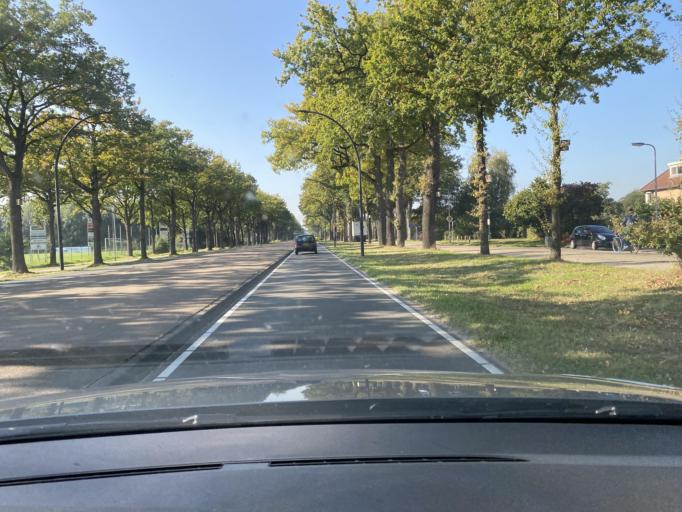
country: NL
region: Overijssel
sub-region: Gemeente Enschede
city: Enschede
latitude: 52.2162
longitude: 6.9590
